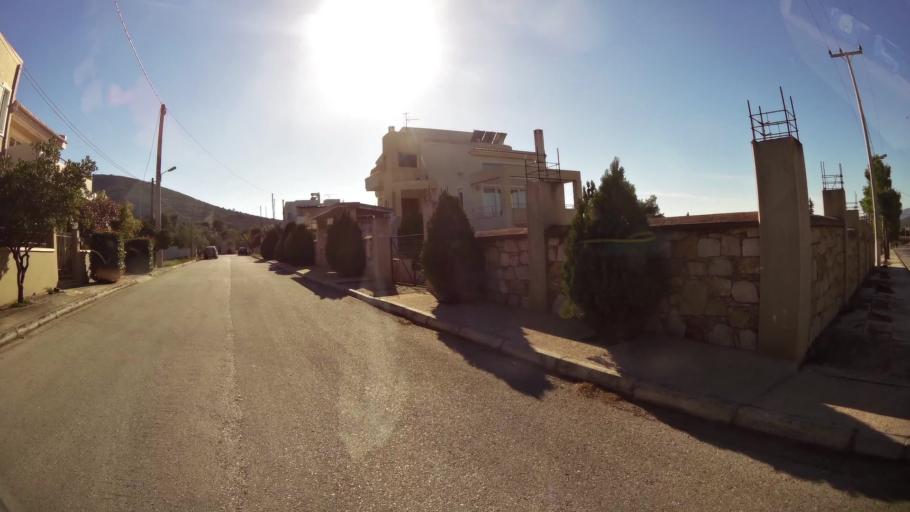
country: GR
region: Attica
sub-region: Nomarchia Anatolikis Attikis
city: Kalyvia Thorikou
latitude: 37.8343
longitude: 23.9271
